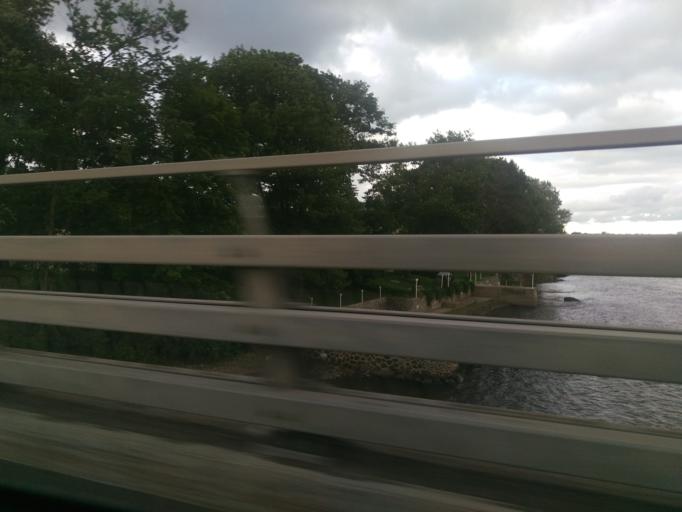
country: CA
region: Quebec
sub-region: Outaouais
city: Gatineau
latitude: 45.4874
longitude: -75.7480
